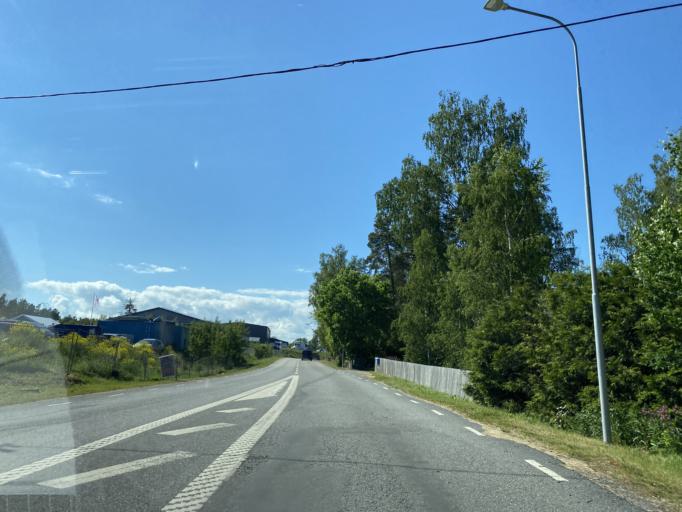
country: SE
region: Stockholm
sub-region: Norrtalje Kommun
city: Norrtalje
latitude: 59.7685
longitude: 18.6896
